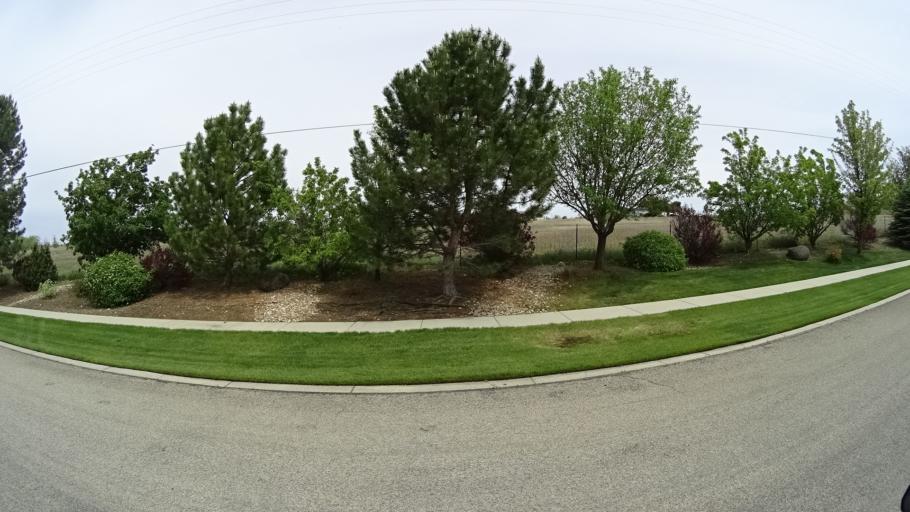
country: US
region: Idaho
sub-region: Ada County
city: Kuna
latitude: 43.5391
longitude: -116.3958
